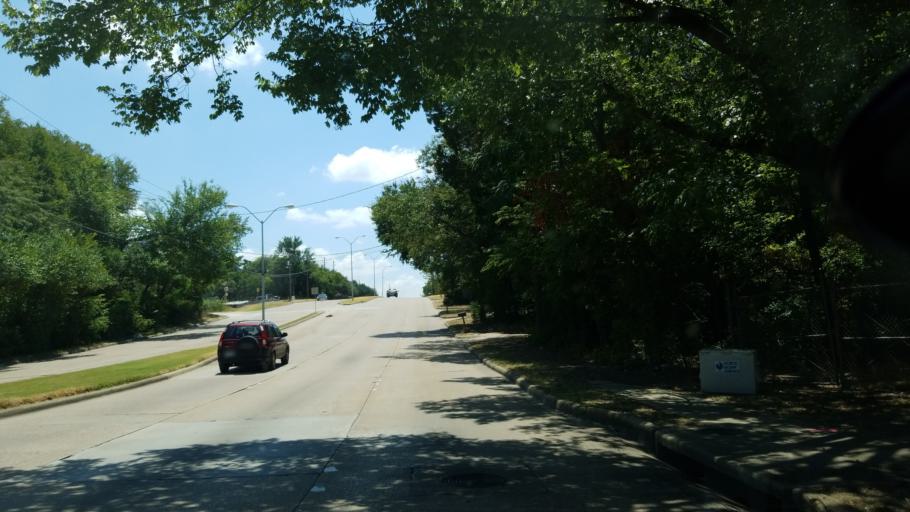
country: US
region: Texas
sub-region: Dallas County
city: Duncanville
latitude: 32.6711
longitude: -96.8915
